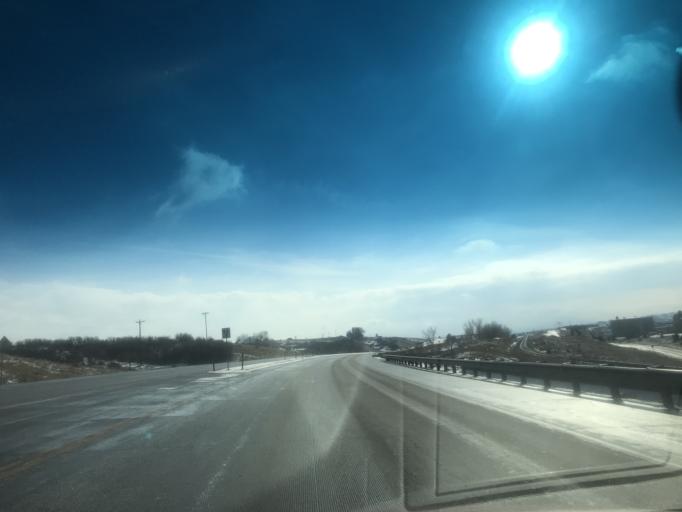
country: US
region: Colorado
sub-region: Douglas County
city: Castle Pines
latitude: 39.4517
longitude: -104.9769
